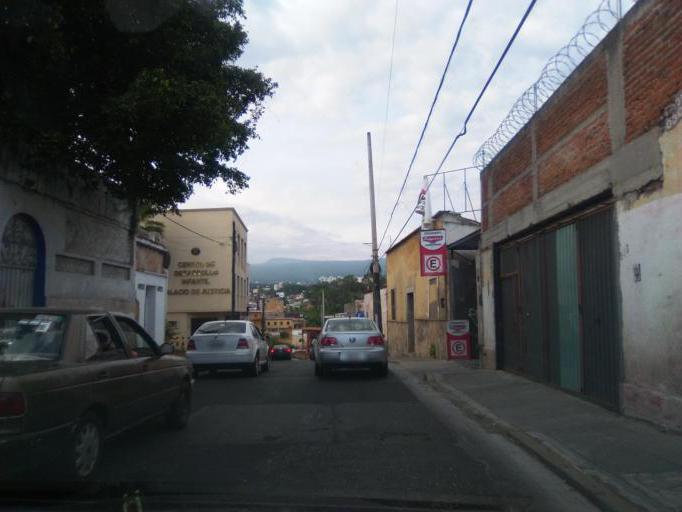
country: MX
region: Morelos
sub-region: Cuernavaca
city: Cuernavaca
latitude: 18.9205
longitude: -99.2312
